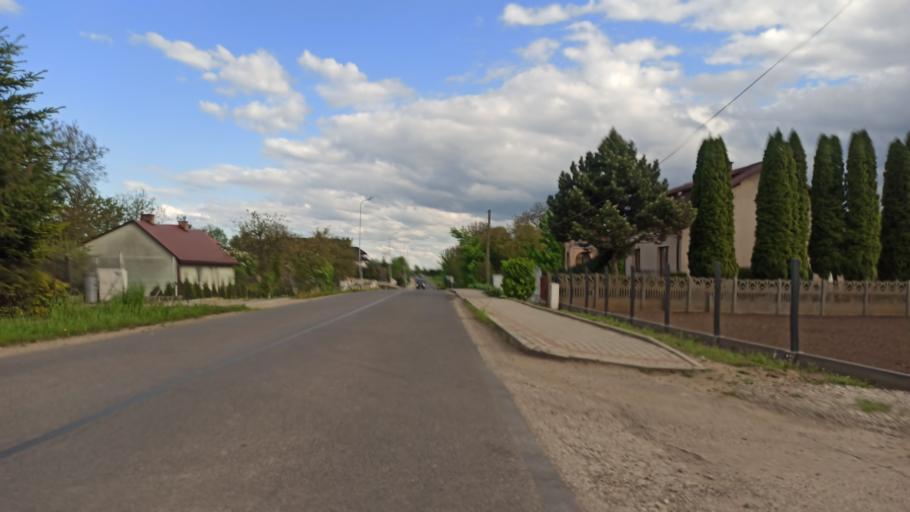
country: PL
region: Subcarpathian Voivodeship
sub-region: Powiat jaroslawski
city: Radymno
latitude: 49.9294
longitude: 22.8438
